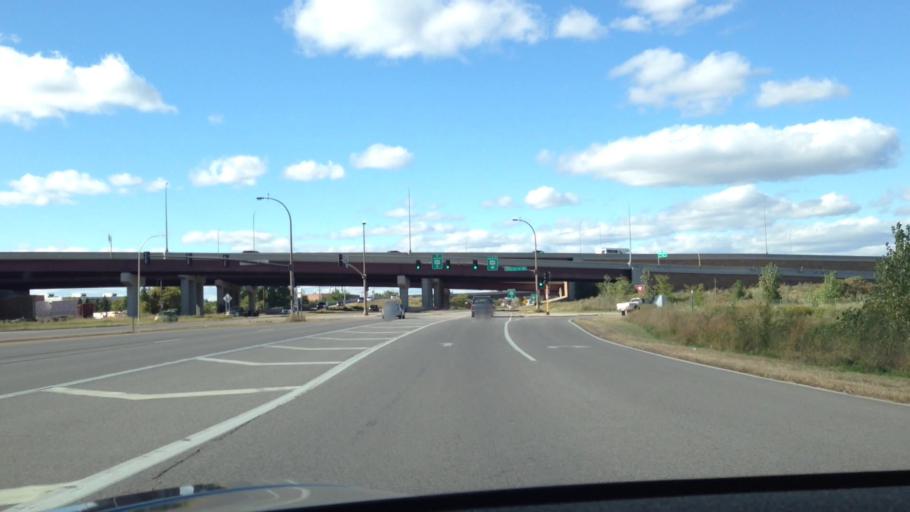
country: US
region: Minnesota
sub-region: Hennepin County
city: Osseo
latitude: 45.1044
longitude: -93.3916
